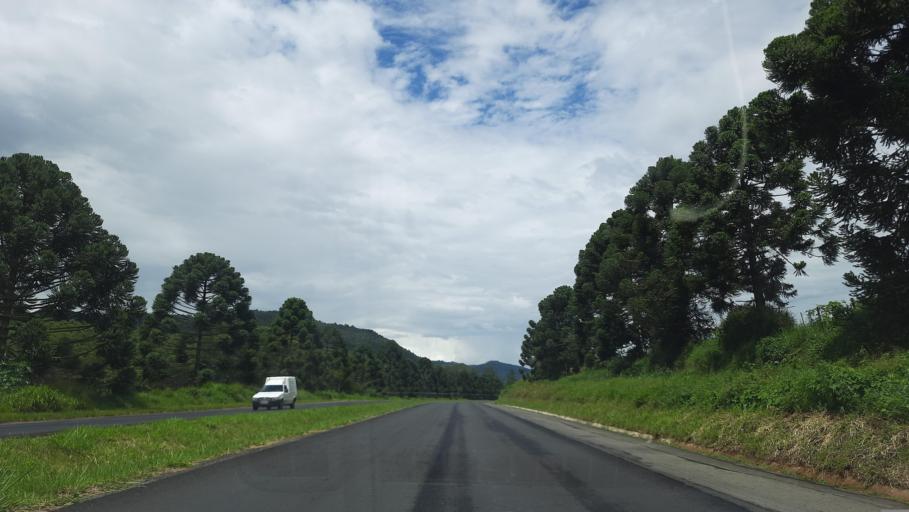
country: BR
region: Minas Gerais
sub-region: Pocos De Caldas
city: Pocos de Caldas
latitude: -21.8136
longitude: -46.6595
